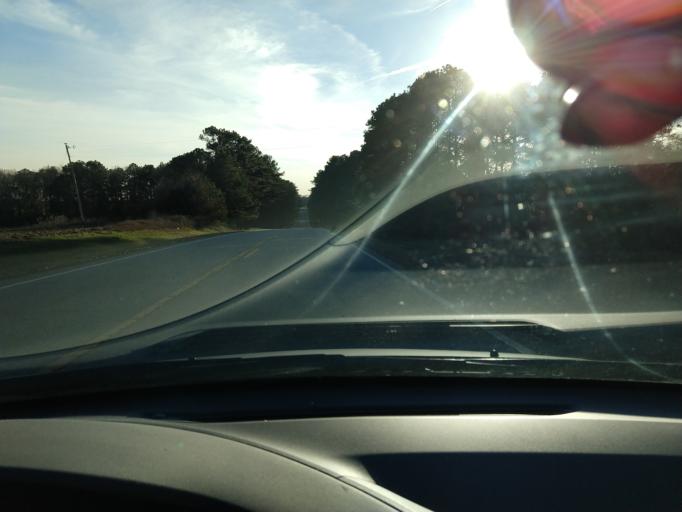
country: US
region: Georgia
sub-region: Sumter County
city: Americus
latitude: 32.1324
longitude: -84.1495
